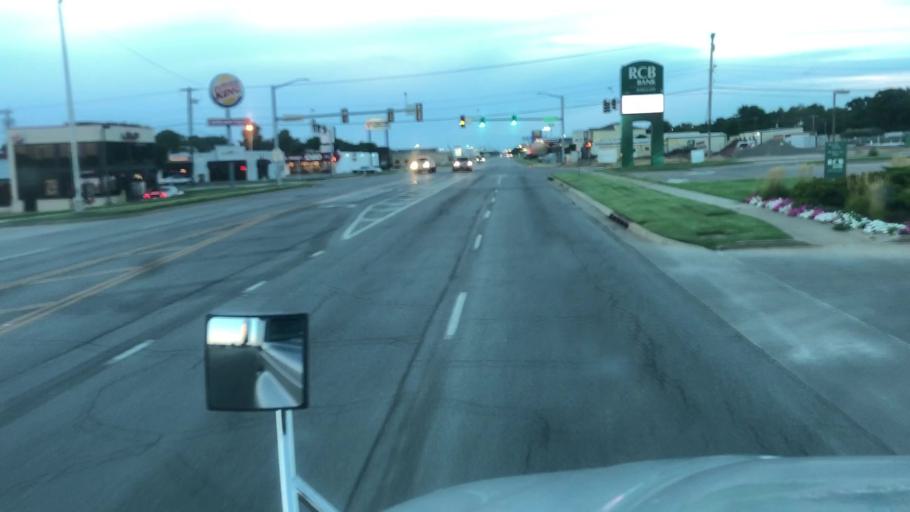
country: US
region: Oklahoma
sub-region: Kay County
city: Ponca City
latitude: 36.7378
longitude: -97.0672
